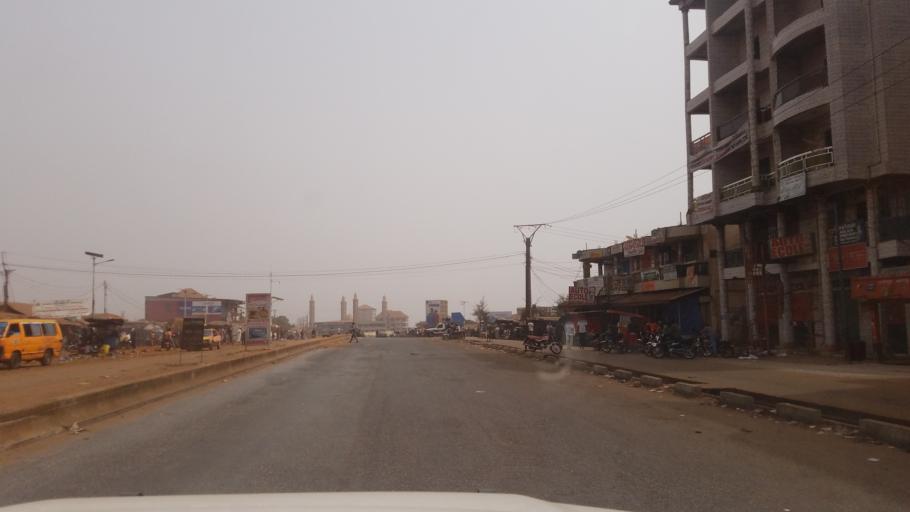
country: GN
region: Kindia
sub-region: Prefecture de Dubreka
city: Dubreka
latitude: 9.6811
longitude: -13.5350
